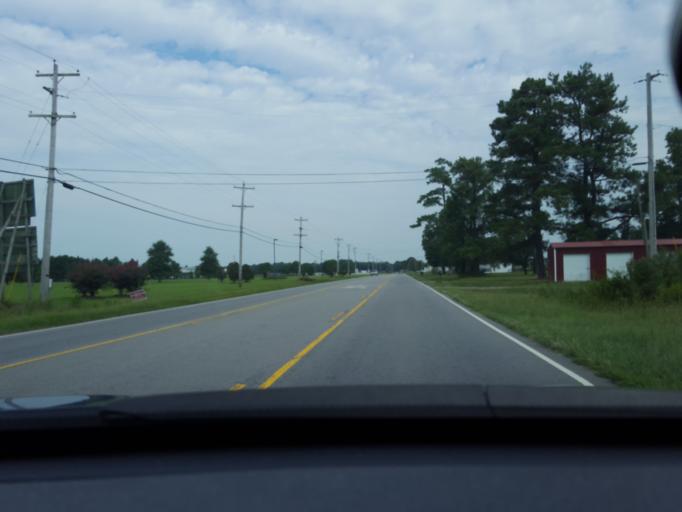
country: US
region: North Carolina
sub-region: Chowan County
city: Edenton
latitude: 36.0876
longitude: -76.6297
